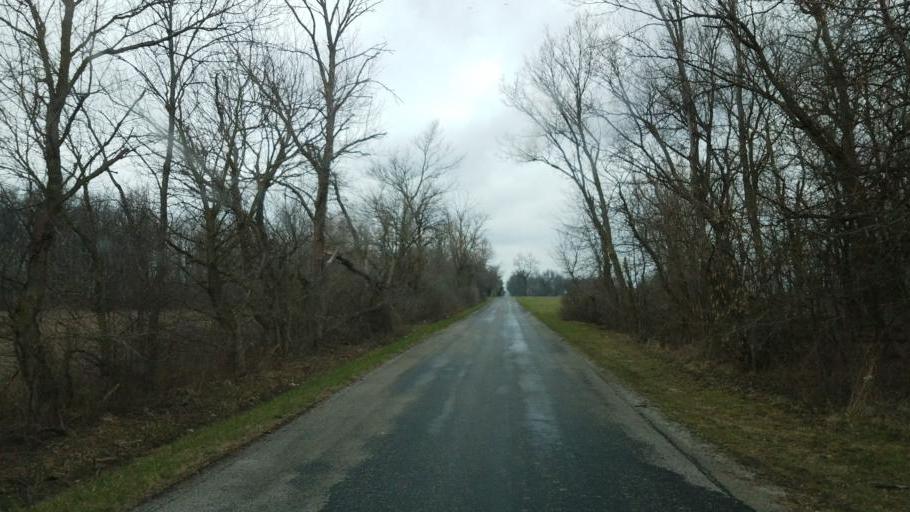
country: US
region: Ohio
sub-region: Delaware County
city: Ashley
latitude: 40.3630
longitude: -82.9872
